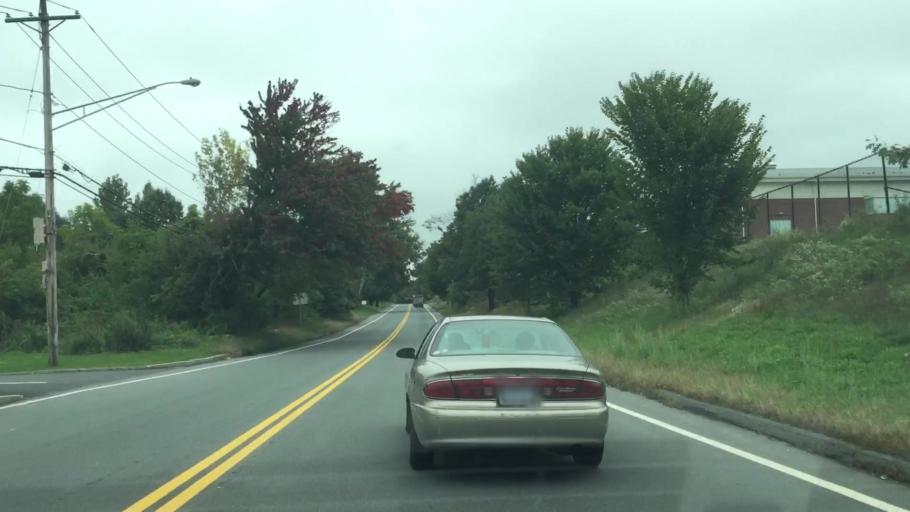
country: US
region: Massachusetts
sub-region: Essex County
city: North Andover
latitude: 42.6996
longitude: -71.1182
